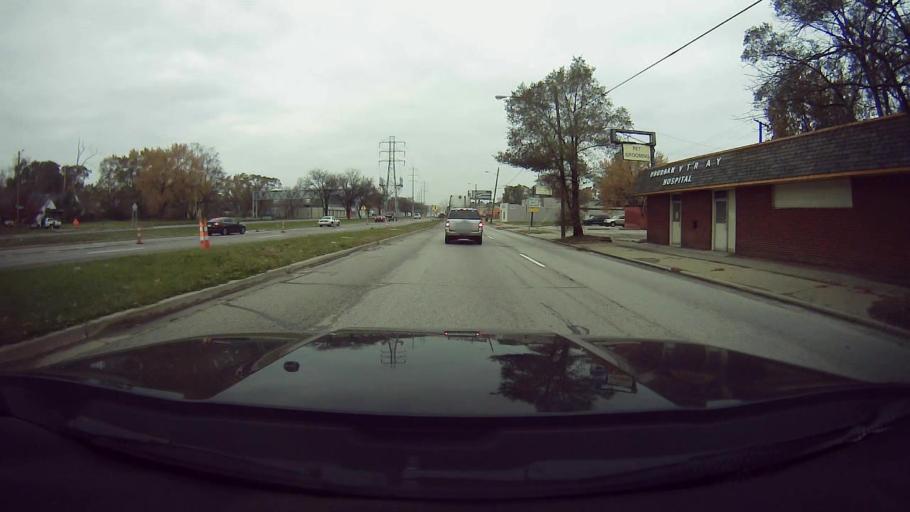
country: US
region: Michigan
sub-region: Oakland County
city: Hazel Park
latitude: 42.4472
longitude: -83.0992
